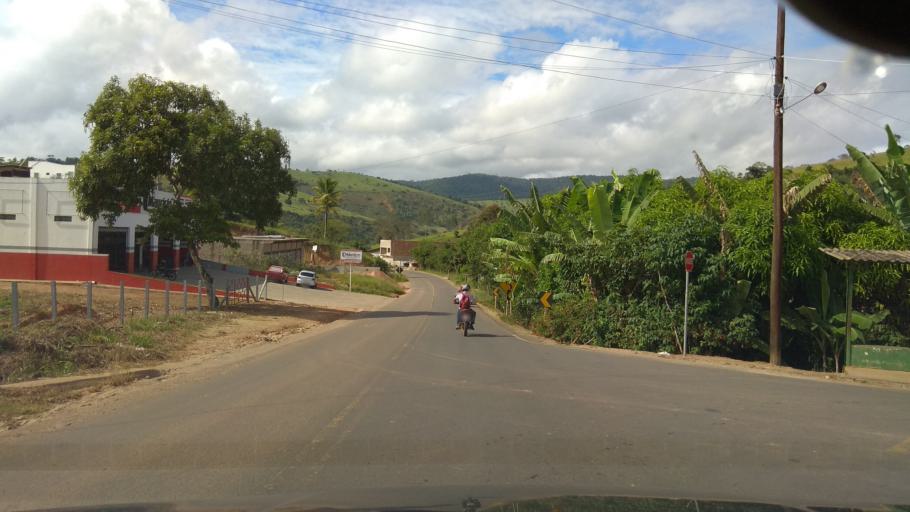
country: BR
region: Bahia
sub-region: Ubaira
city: Ubaira
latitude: -13.2696
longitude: -39.6586
